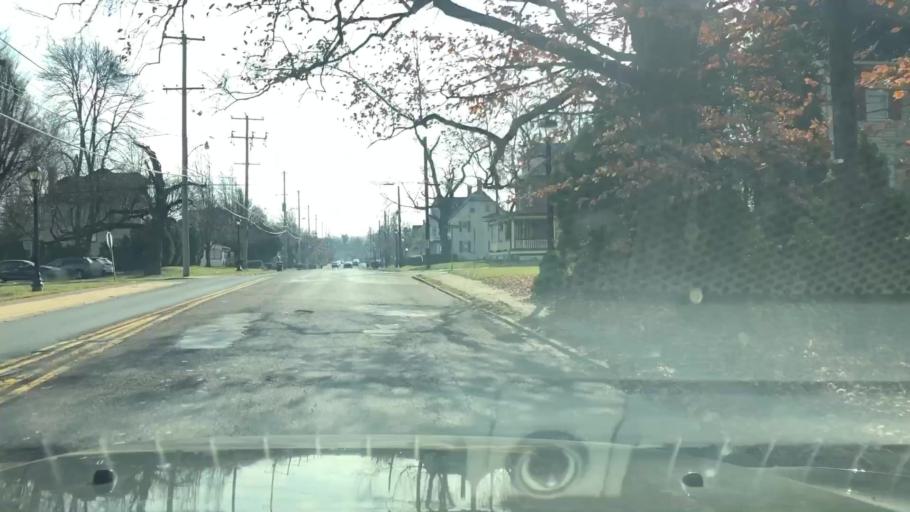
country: US
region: Pennsylvania
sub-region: Bucks County
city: Langhorne
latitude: 40.1810
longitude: -74.9187
